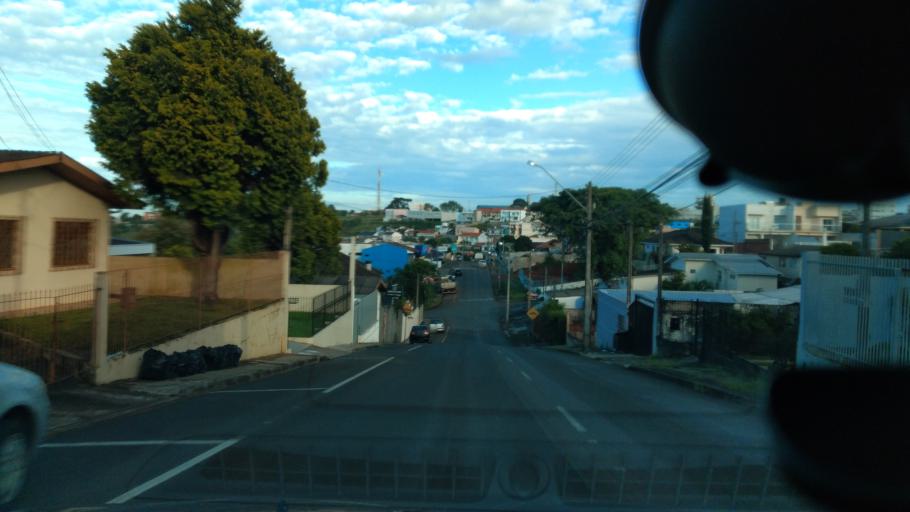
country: BR
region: Parana
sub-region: Guarapuava
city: Guarapuava
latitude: -25.3828
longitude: -51.4734
